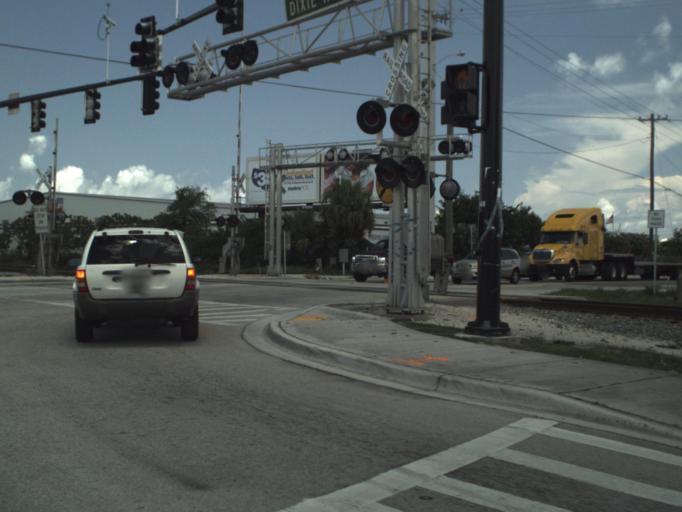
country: US
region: Florida
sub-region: Broward County
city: Pompano Beach Highlands
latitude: 26.2898
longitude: -80.1095
